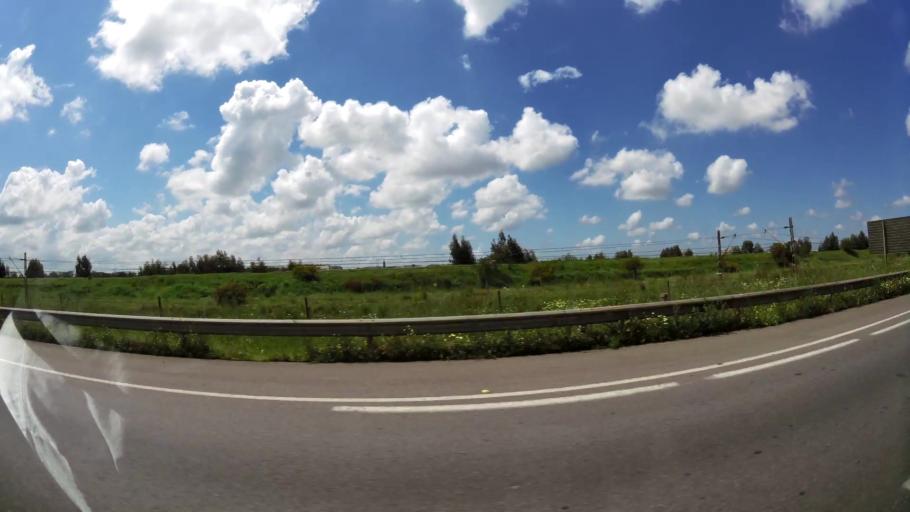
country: MA
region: Grand Casablanca
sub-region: Nouaceur
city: Bouskoura
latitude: 33.4297
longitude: -7.6278
